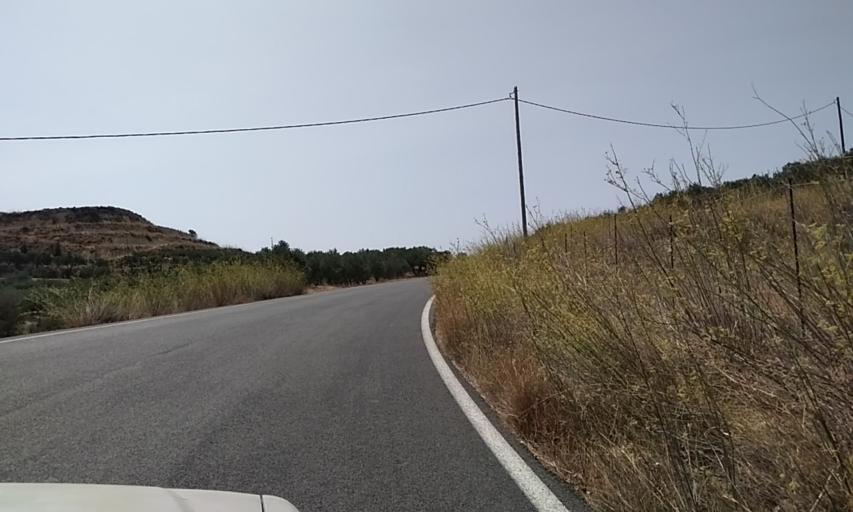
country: GR
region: Crete
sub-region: Nomos Lasithiou
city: Siteia
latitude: 35.1107
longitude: 26.0579
